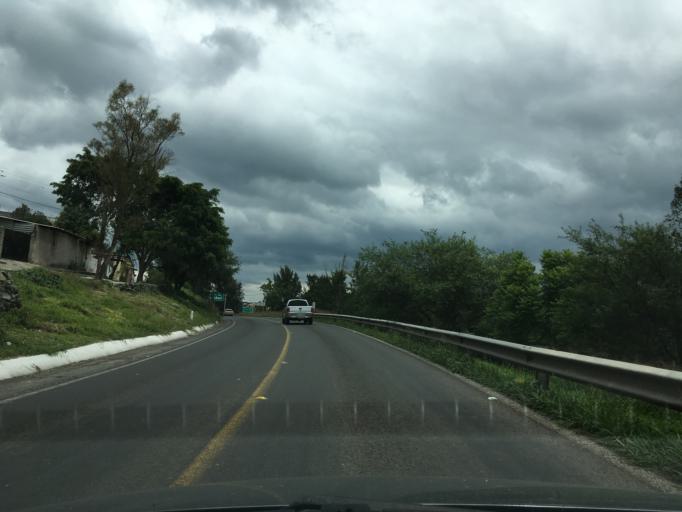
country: MX
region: Guanajuato
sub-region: Moroleon
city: Rinconadas del Bosque
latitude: 20.0834
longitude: -101.1559
